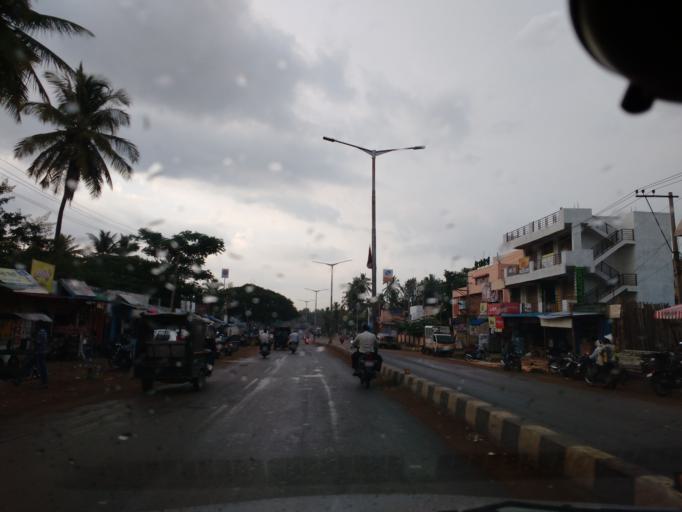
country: IN
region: Karnataka
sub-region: Tumkur
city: Tiptur
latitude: 13.2584
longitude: 76.4842
